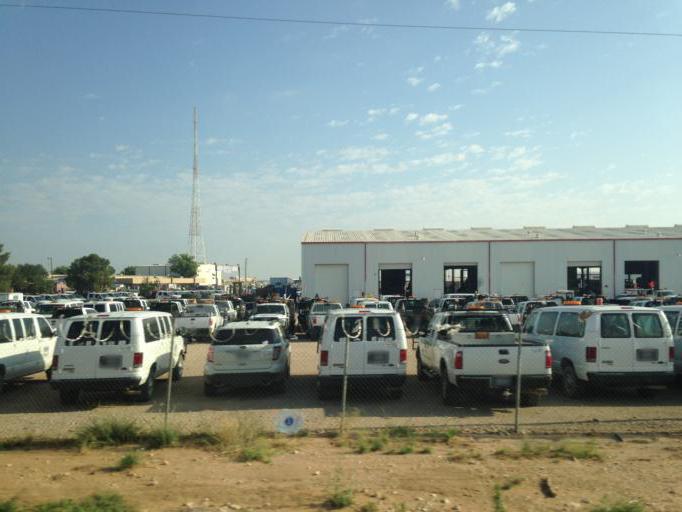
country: US
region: Texas
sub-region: Midland County
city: Midland
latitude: 31.9507
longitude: -102.1414
